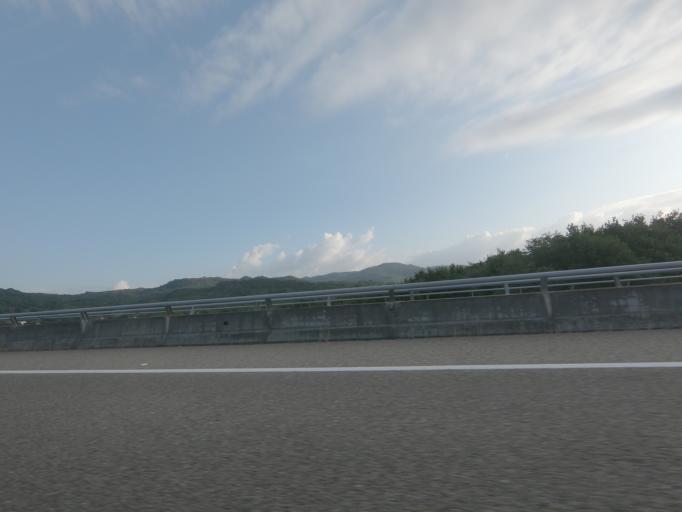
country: ES
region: Galicia
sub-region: Provincia de Ourense
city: Allariz
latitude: 42.1971
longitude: -7.7798
